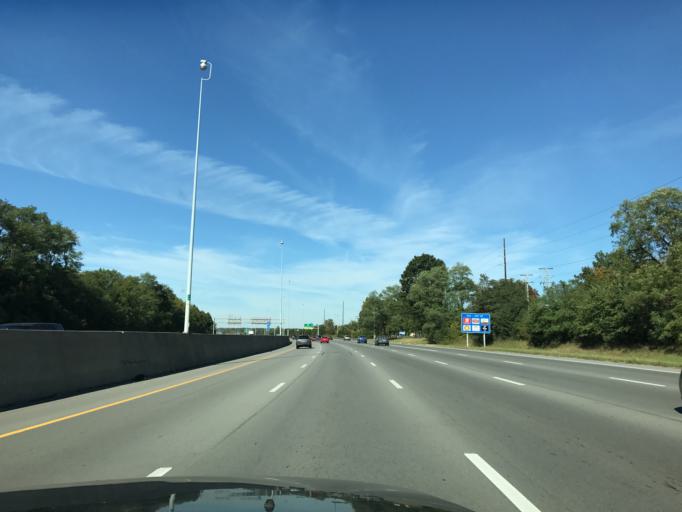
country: US
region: Ohio
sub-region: Franklin County
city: Huber Ridge
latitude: 40.0984
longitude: -82.9155
